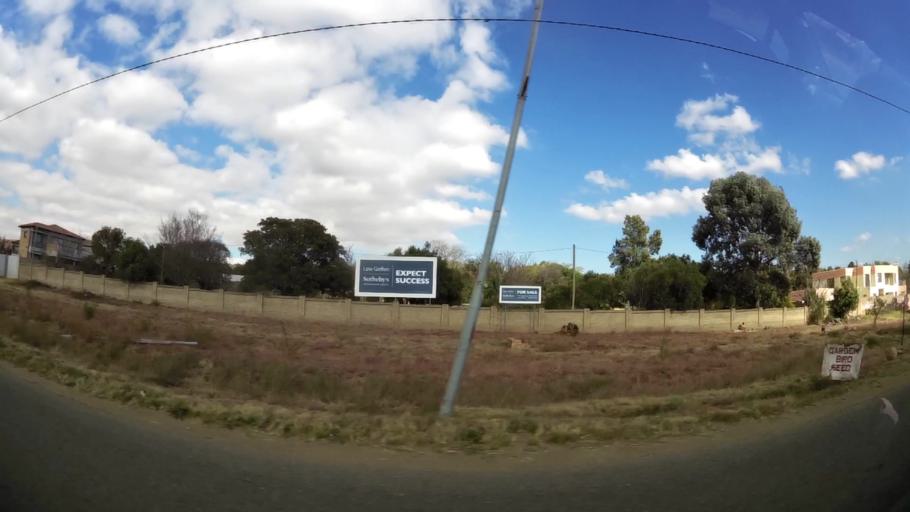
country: ZA
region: Gauteng
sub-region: West Rand District Municipality
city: Muldersdriseloop
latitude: -26.0771
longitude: 27.8570
